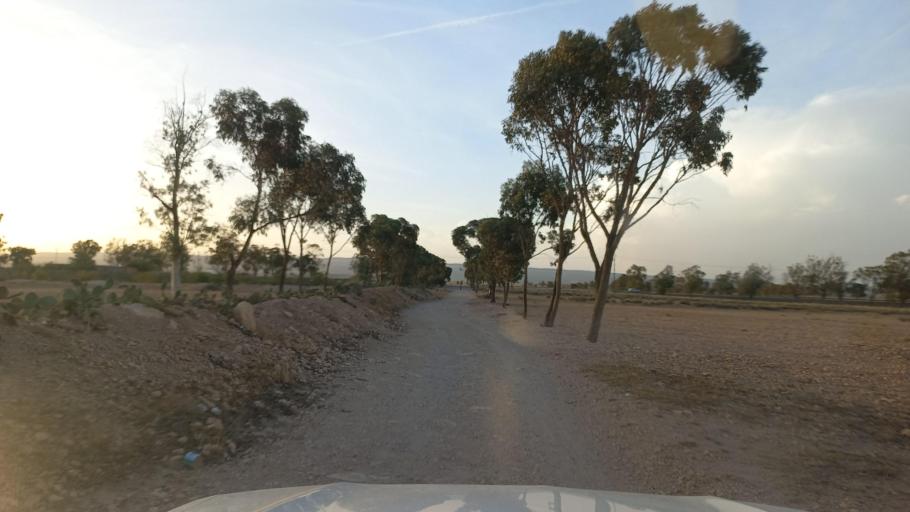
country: TN
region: Al Qasrayn
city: Kasserine
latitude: 35.2412
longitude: 8.9931
